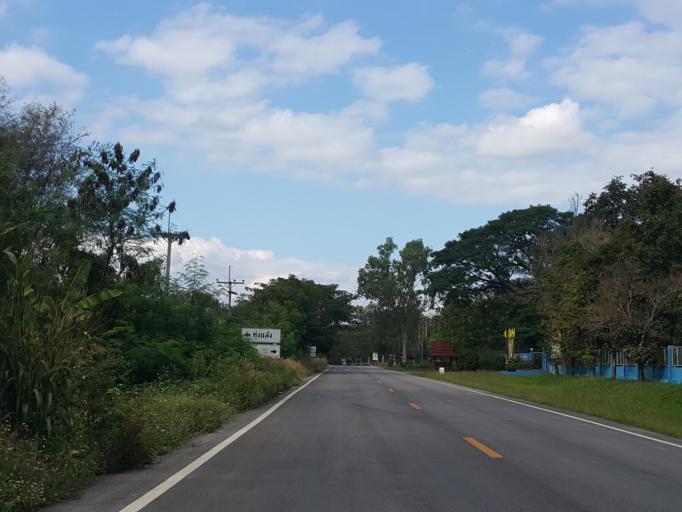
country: TH
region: Lampang
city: Chae Hom
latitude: 18.6482
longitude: 99.4939
